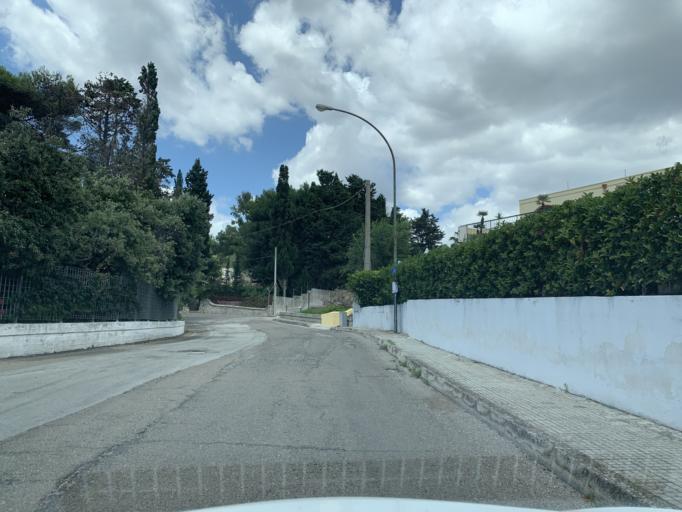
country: IT
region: Apulia
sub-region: Provincia di Lecce
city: Santa Cesarea Terme
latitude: 40.0332
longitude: 18.4470
